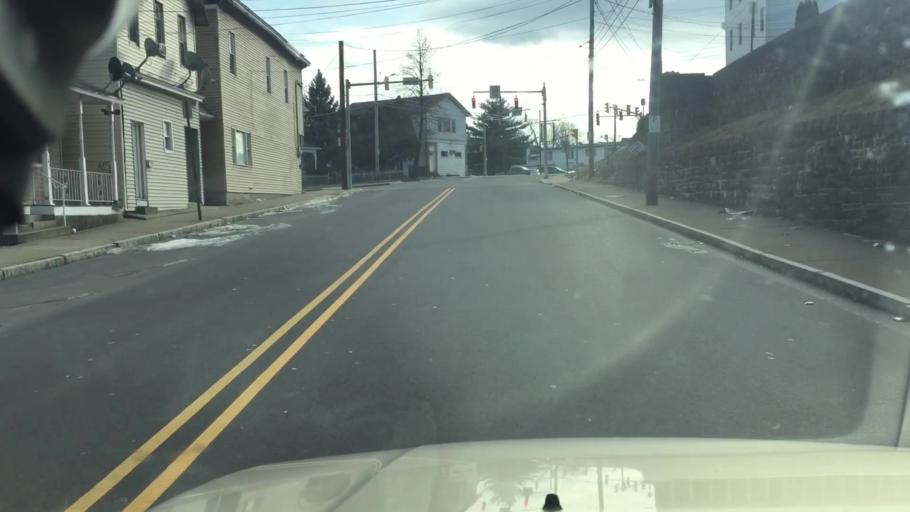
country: US
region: Pennsylvania
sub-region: Luzerne County
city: Wilkes-Barre
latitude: 41.2317
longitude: -75.8908
